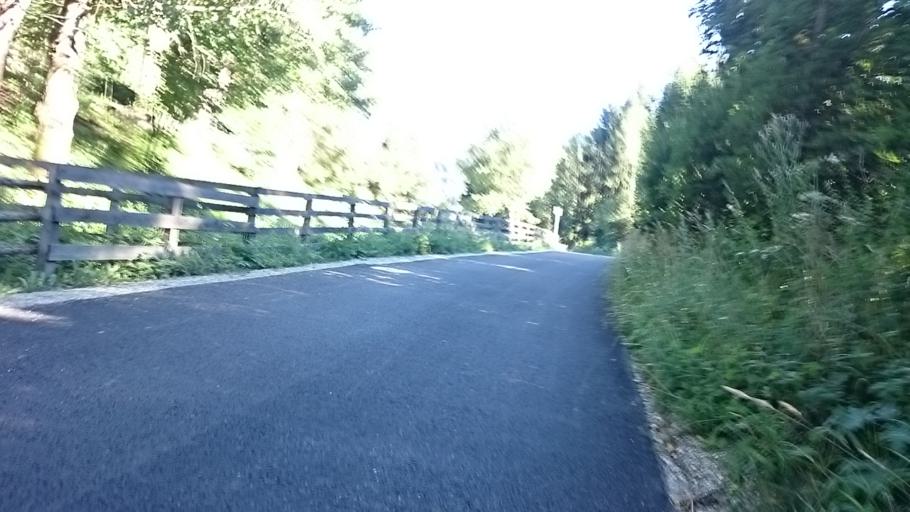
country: IT
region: Trentino-Alto Adige
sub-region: Bolzano
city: Monguelfo
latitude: 46.7467
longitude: 12.1190
